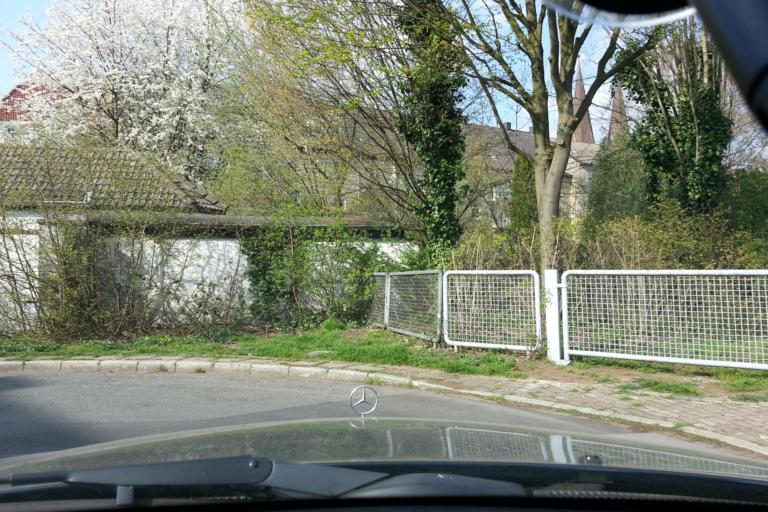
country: DE
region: North Rhine-Westphalia
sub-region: Regierungsbezirk Arnsberg
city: Herne
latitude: 51.5442
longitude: 7.2076
